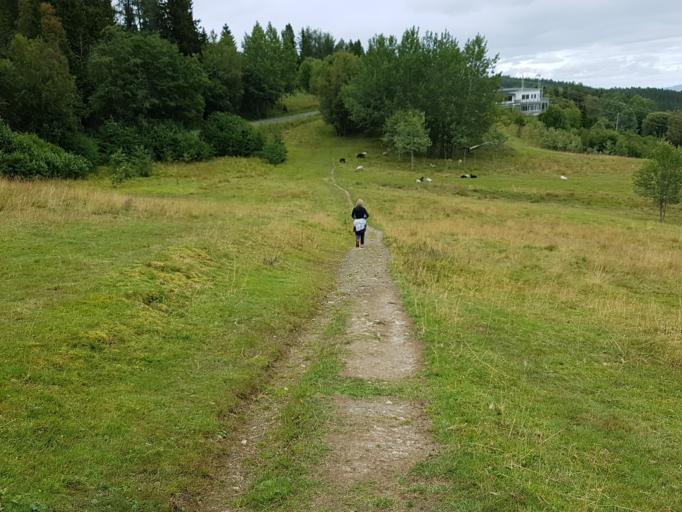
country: NO
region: Sor-Trondelag
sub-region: Trondheim
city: Trondheim
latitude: 63.4007
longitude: 10.3082
